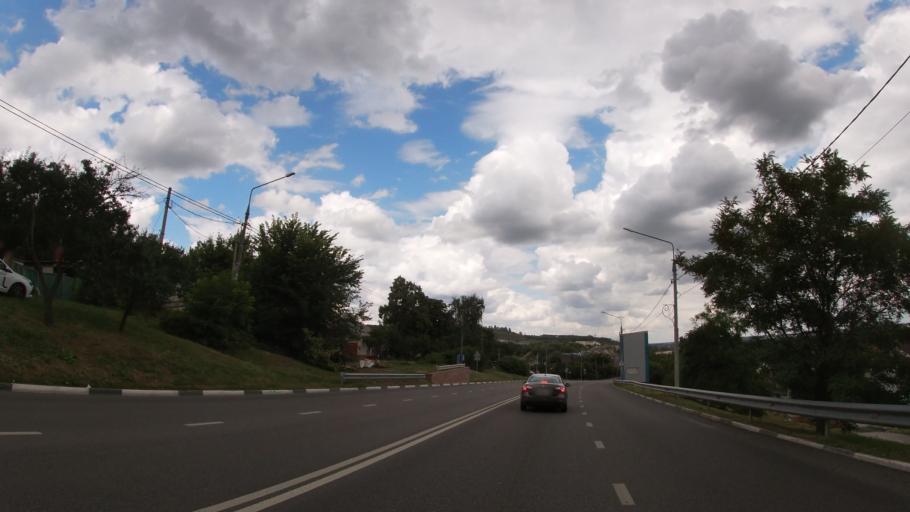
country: RU
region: Belgorod
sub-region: Belgorodskiy Rayon
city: Belgorod
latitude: 50.6045
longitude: 36.6105
